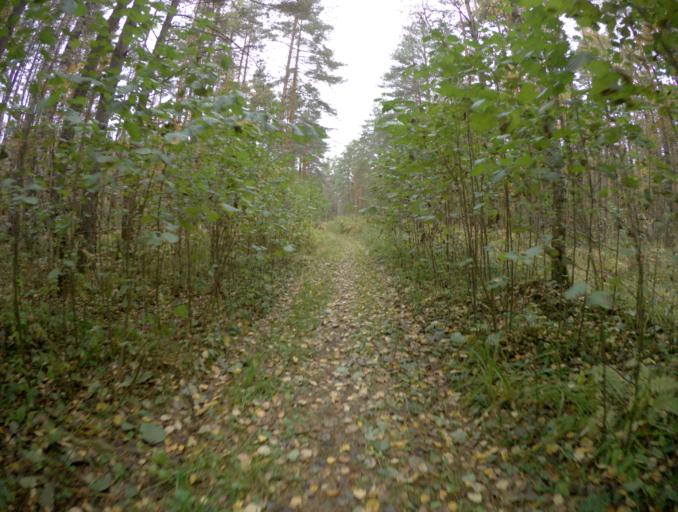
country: RU
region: Vladimir
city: Kommunar
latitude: 56.0803
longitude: 40.4407
